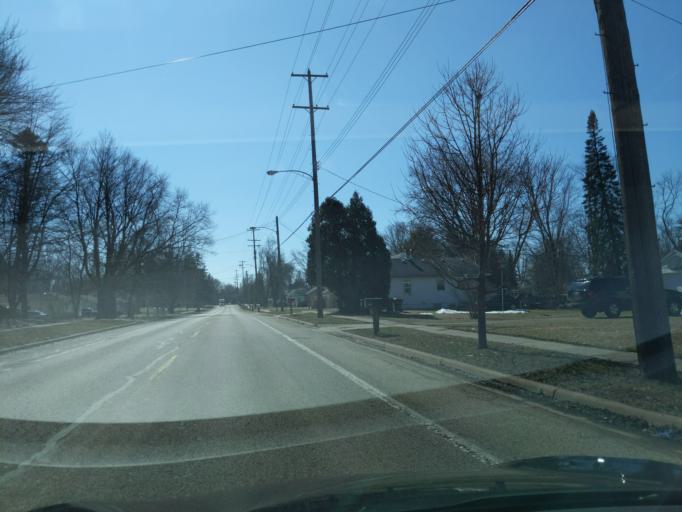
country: US
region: Michigan
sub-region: Ingham County
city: Holt
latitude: 42.6678
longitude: -84.5629
